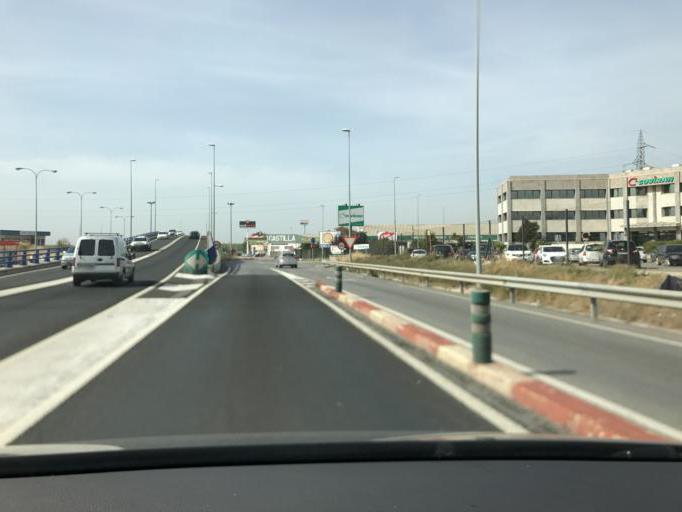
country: ES
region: Andalusia
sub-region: Provincia de Granada
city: Albolote
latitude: 37.2055
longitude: -3.6638
